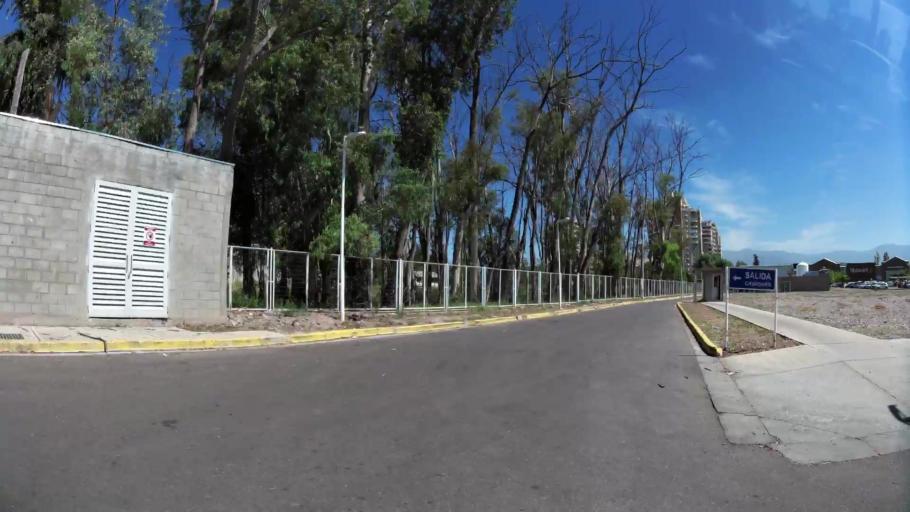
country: AR
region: Mendoza
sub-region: Departamento de Godoy Cruz
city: Godoy Cruz
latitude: -32.9525
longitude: -68.8559
